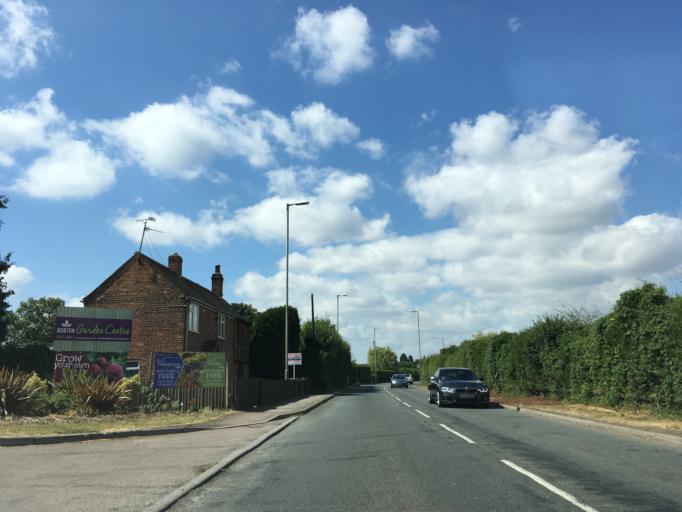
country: GB
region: England
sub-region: Gloucestershire
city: Barnwood
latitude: 51.9015
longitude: -2.2175
